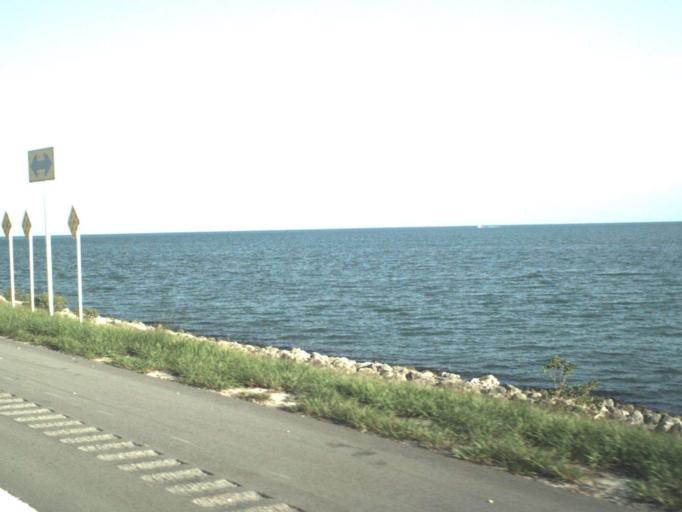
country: US
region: Florida
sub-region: Monroe County
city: Islamorada
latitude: 24.8399
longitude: -80.7820
